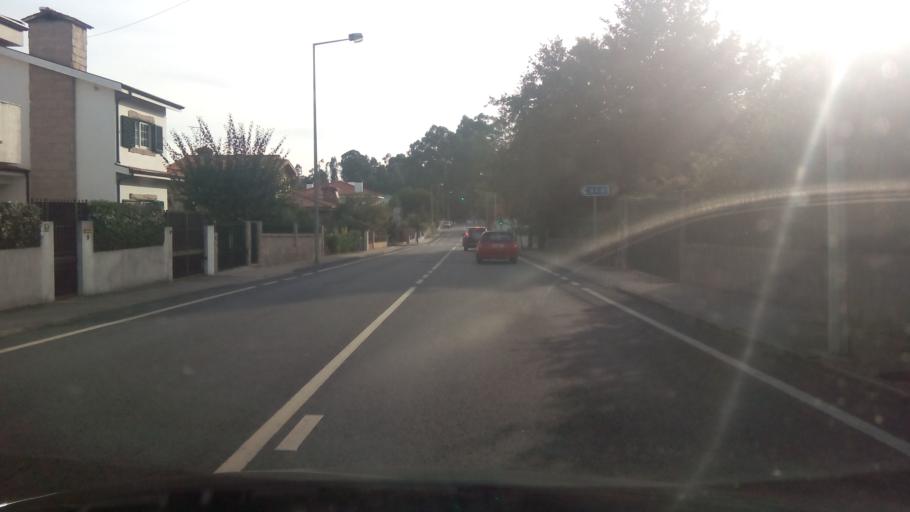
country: PT
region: Porto
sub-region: Paredes
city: Casteloes de Cepeda
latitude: 41.2083
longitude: -8.3395
